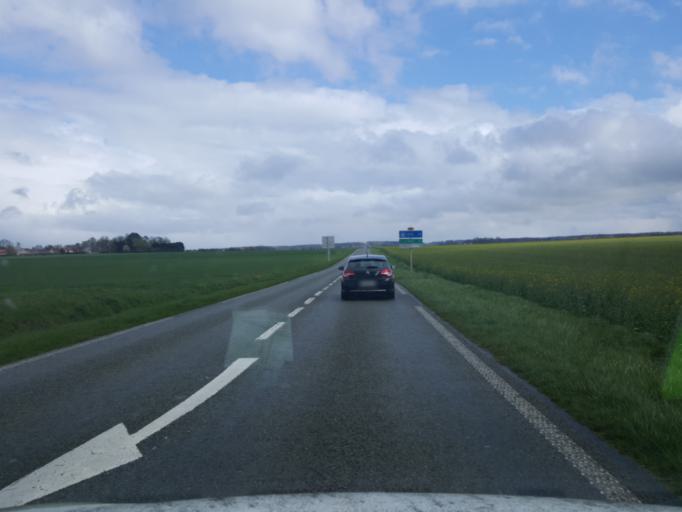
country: FR
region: Picardie
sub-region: Departement de l'Oise
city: Chaumont-en-Vexin
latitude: 49.3188
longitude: 1.8887
